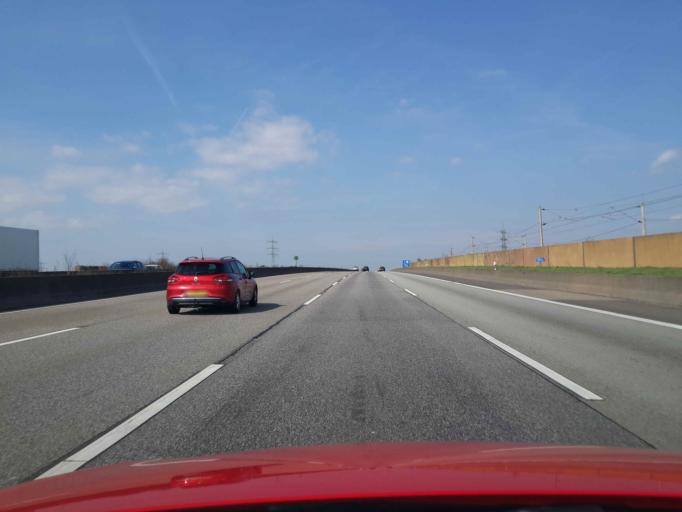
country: DE
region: Hesse
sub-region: Regierungsbezirk Darmstadt
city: Florsheim
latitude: 50.0395
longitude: 8.4237
